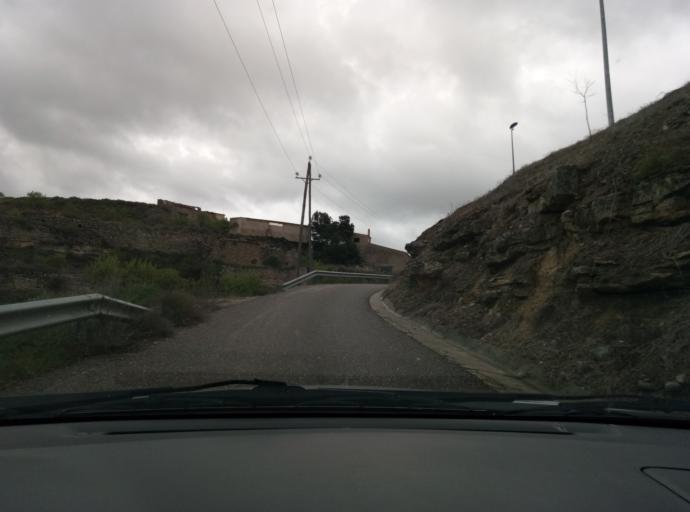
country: ES
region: Catalonia
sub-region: Provincia de Lleida
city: Guimera
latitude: 41.5654
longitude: 1.1856
